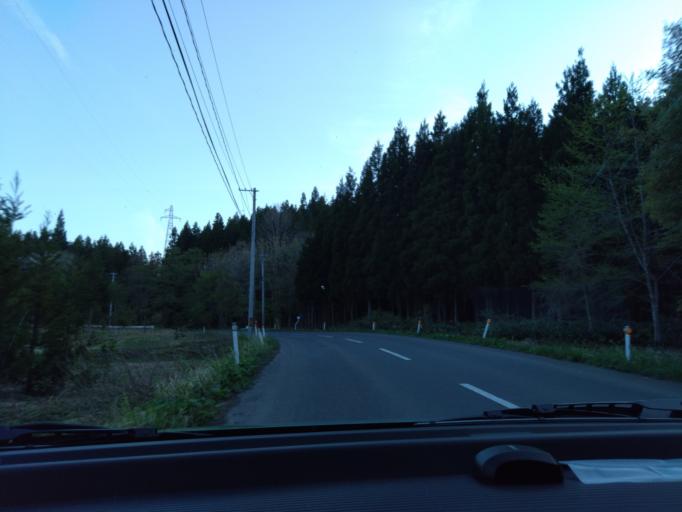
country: JP
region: Iwate
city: Kitakami
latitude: 39.2553
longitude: 140.9811
